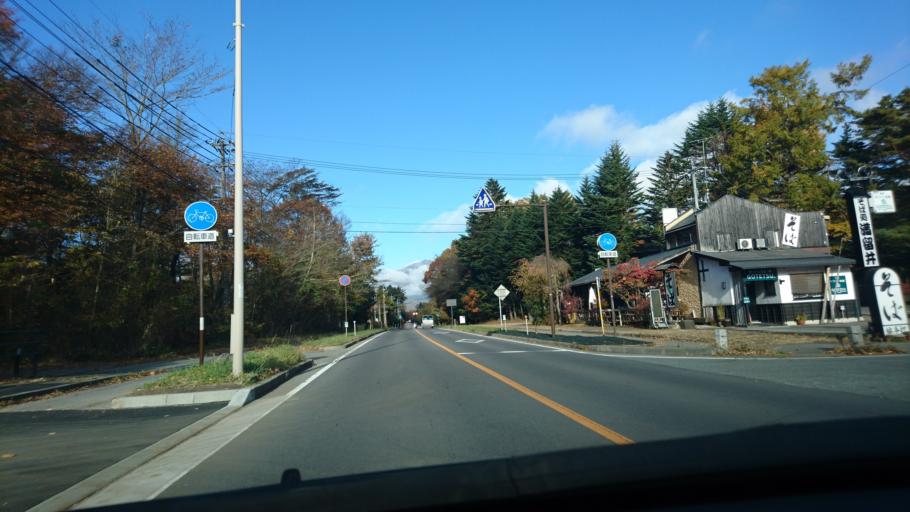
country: JP
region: Nagano
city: Saku
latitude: 36.3276
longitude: 138.6152
